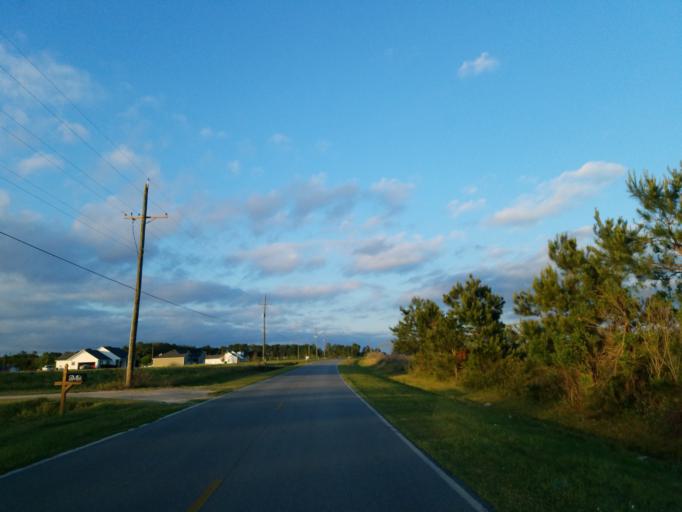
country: US
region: Georgia
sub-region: Lowndes County
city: Hahira
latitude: 31.0606
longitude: -83.3757
